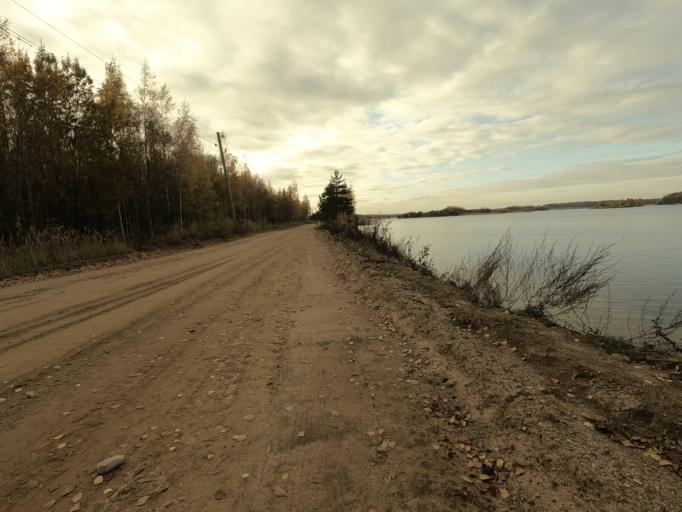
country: RU
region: Leningrad
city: Priladozhskiy
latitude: 59.7133
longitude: 31.3489
